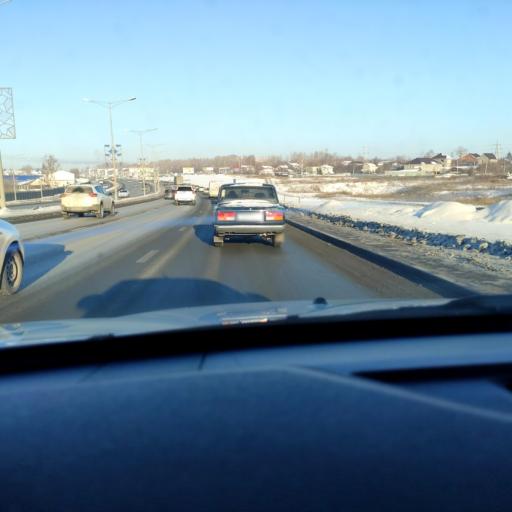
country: RU
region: Samara
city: Petra-Dubrava
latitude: 53.2827
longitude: 50.2813
